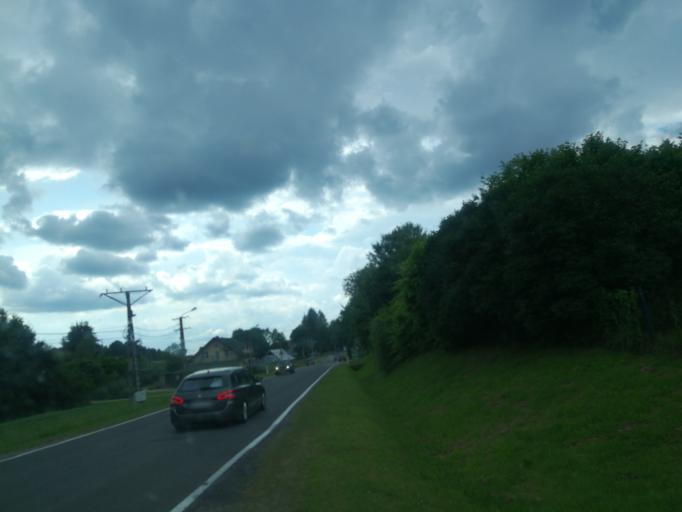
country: PL
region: Subcarpathian Voivodeship
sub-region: Powiat leski
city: Olszanica
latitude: 49.4432
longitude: 22.4492
